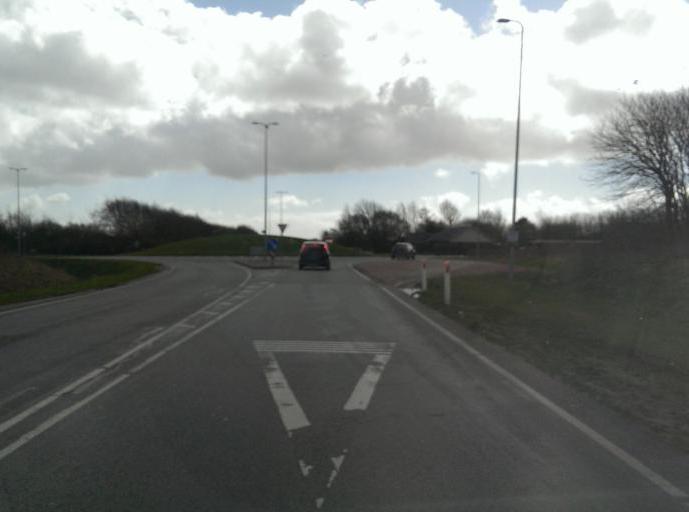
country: DK
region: South Denmark
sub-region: Esbjerg Kommune
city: Esbjerg
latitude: 55.5184
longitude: 8.4066
